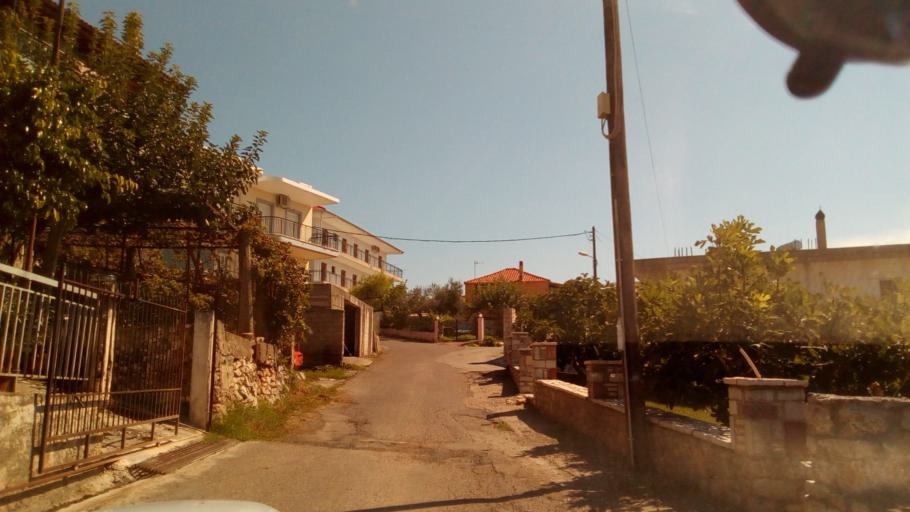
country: GR
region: West Greece
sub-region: Nomos Aitolias kai Akarnanias
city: Nafpaktos
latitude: 38.4165
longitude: 21.8964
